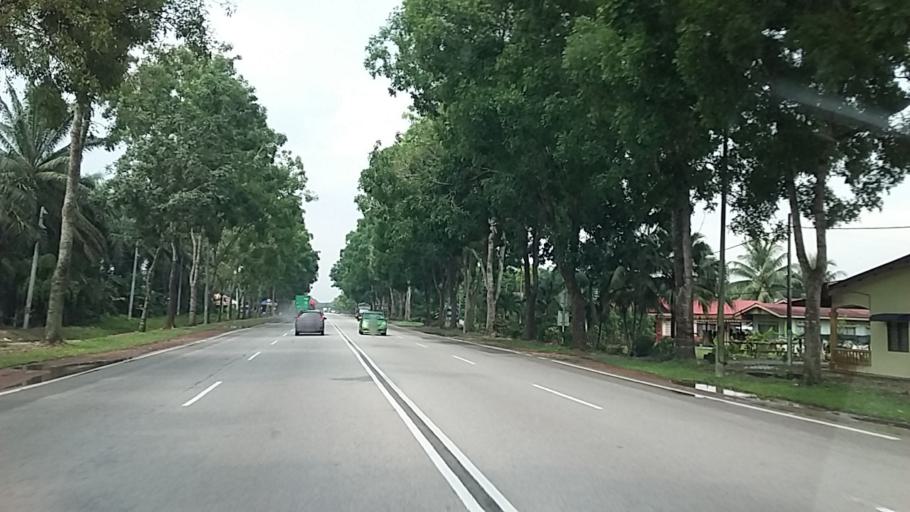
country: MY
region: Johor
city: Parit Raja
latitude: 1.8718
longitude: 103.1313
